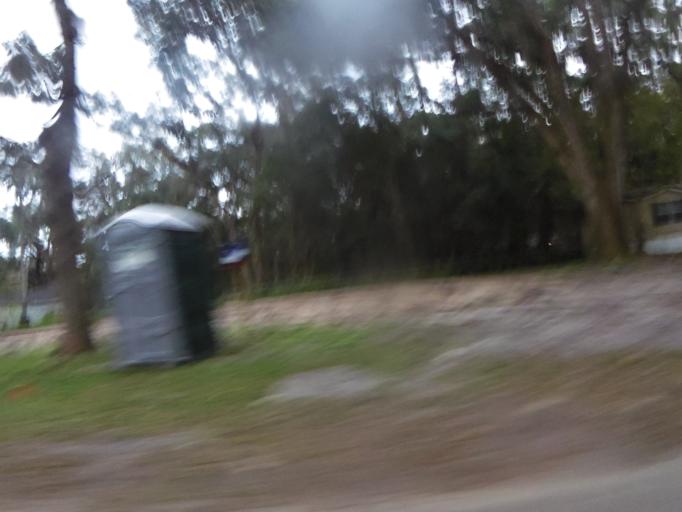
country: US
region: Florida
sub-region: Duval County
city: Jacksonville
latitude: 30.2637
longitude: -81.5823
